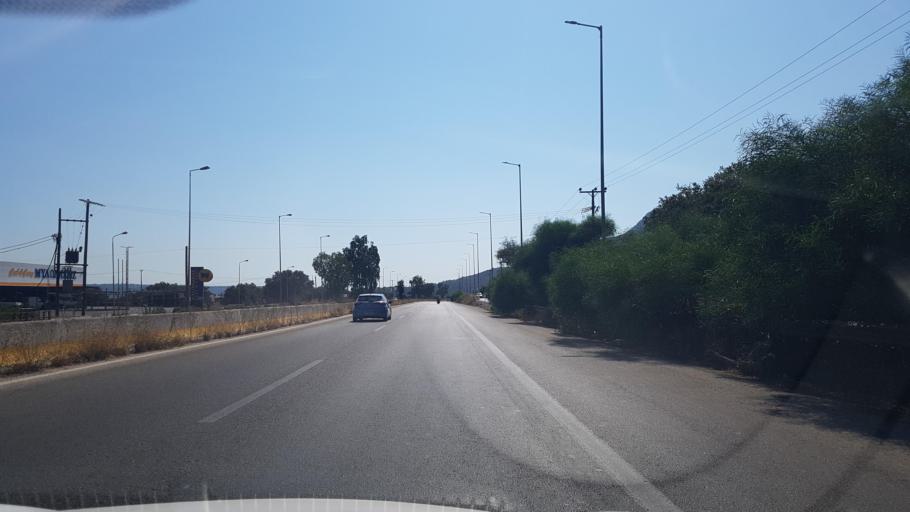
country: GR
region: Crete
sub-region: Nomos Chanias
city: Nerokouros
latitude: 35.4807
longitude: 24.0479
